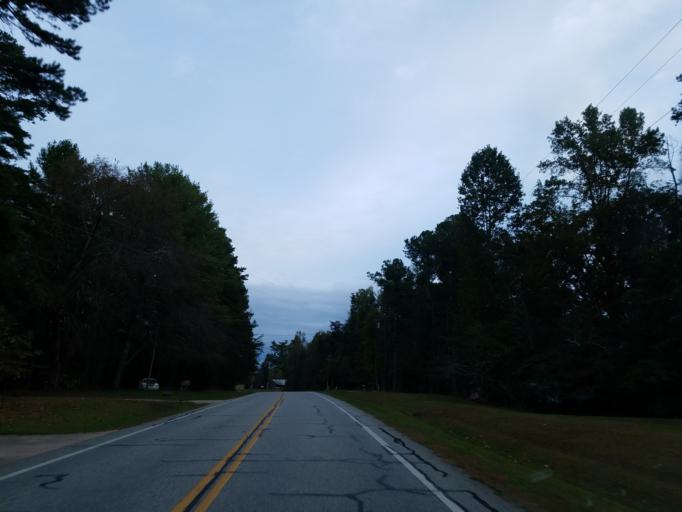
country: US
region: Georgia
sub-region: Dawson County
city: Dawsonville
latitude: 34.4472
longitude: -84.1675
